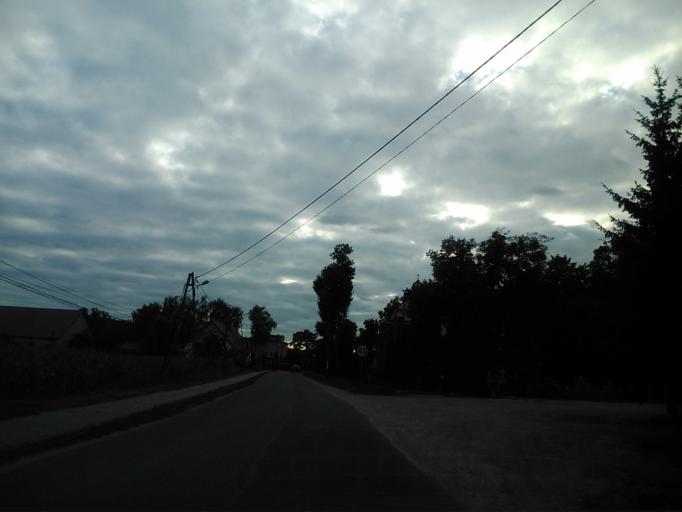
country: PL
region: Kujawsko-Pomorskie
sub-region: Powiat golubsko-dobrzynski
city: Kowalewo Pomorskie
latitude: 53.1439
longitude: 18.9728
